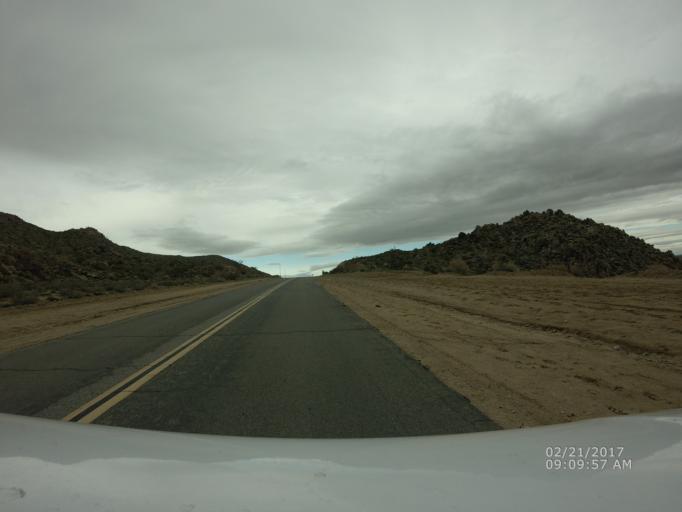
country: US
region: California
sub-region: Los Angeles County
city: Lake Los Angeles
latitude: 34.6082
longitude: -117.8362
